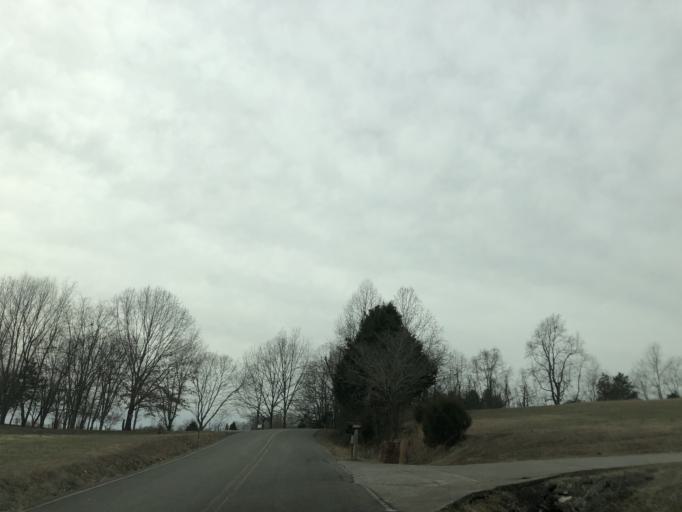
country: US
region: Tennessee
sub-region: Robertson County
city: Greenbrier
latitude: 36.4694
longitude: -86.7955
